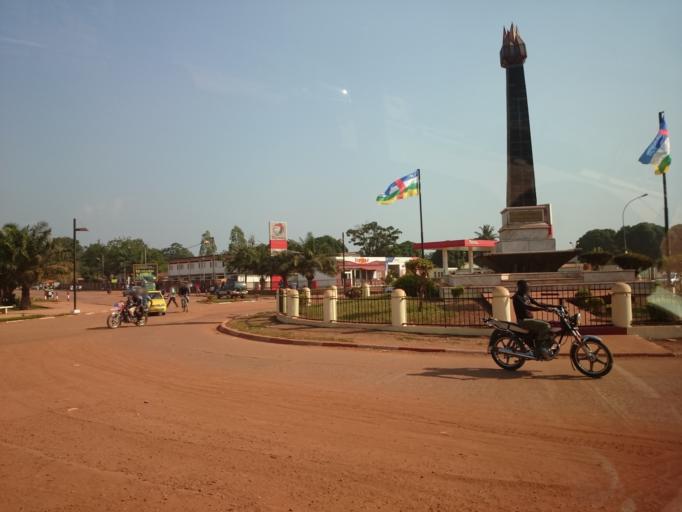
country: CF
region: Bangui
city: Bangui
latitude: 4.3735
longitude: 18.5627
